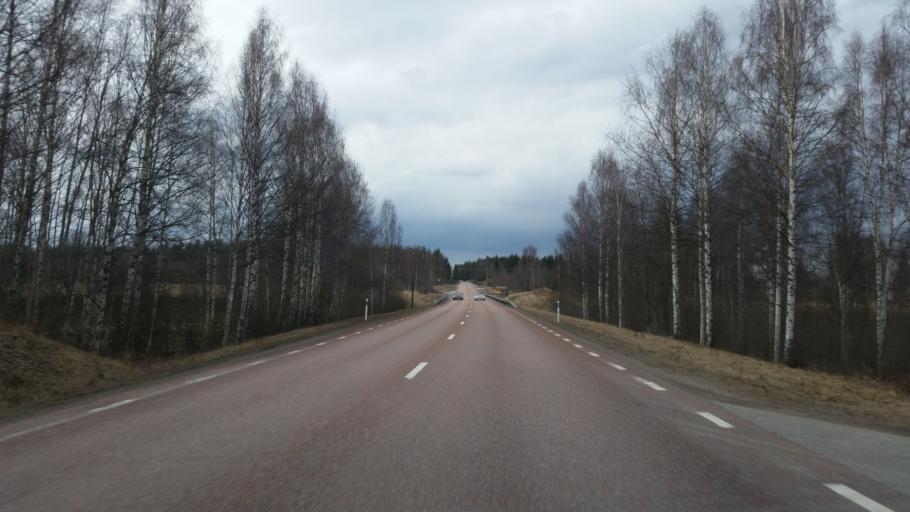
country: SE
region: Gaevleborg
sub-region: Ljusdals Kommun
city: Jaervsoe
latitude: 61.7626
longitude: 16.1593
